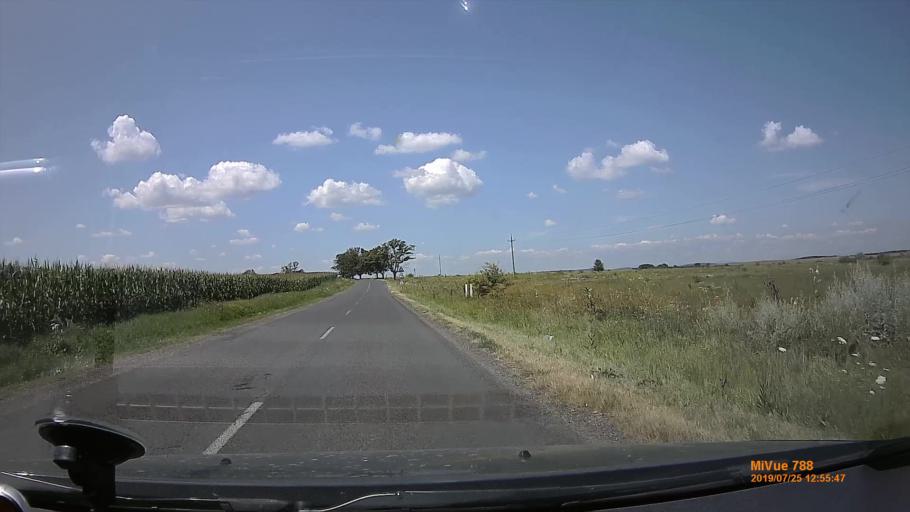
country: HU
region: Borsod-Abauj-Zemplen
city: Abaujszanto
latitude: 48.3115
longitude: 21.1827
